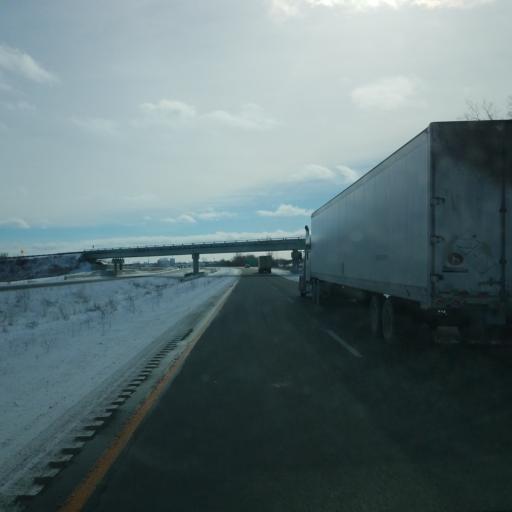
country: US
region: Michigan
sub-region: Gratiot County
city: Ithaca
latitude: 43.3072
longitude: -84.5976
